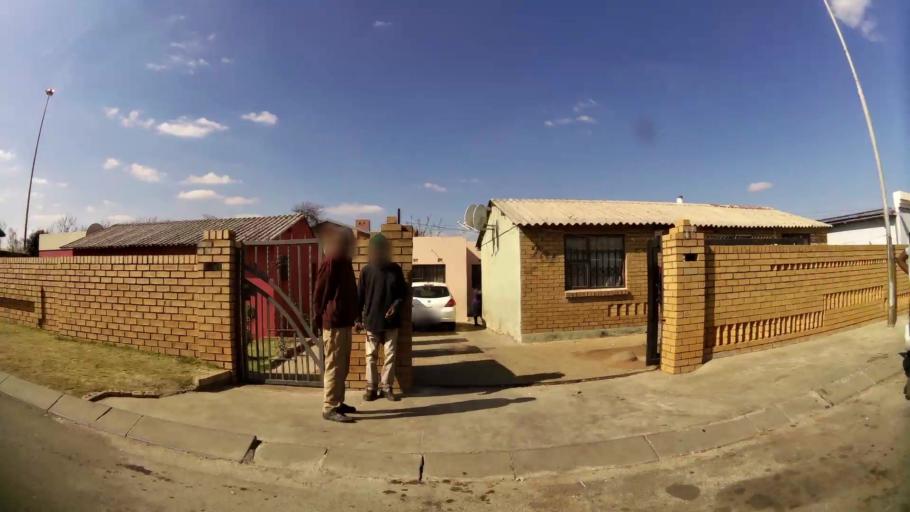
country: ZA
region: Gauteng
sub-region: City of Johannesburg Metropolitan Municipality
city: Soweto
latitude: -26.2566
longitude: 27.8887
